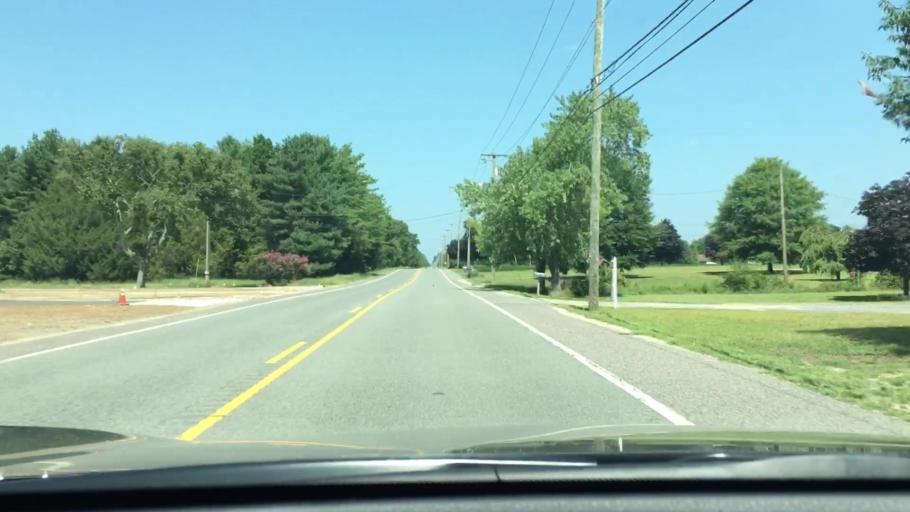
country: US
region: New Jersey
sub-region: Cumberland County
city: Laurel Lake
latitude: 39.2934
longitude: -74.9975
